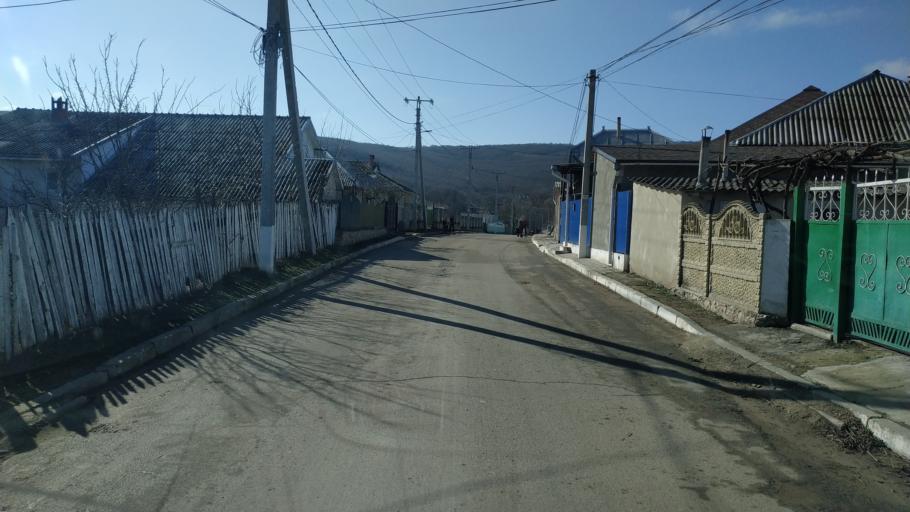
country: MD
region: Hincesti
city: Hincesti
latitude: 46.9217
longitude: 28.6266
